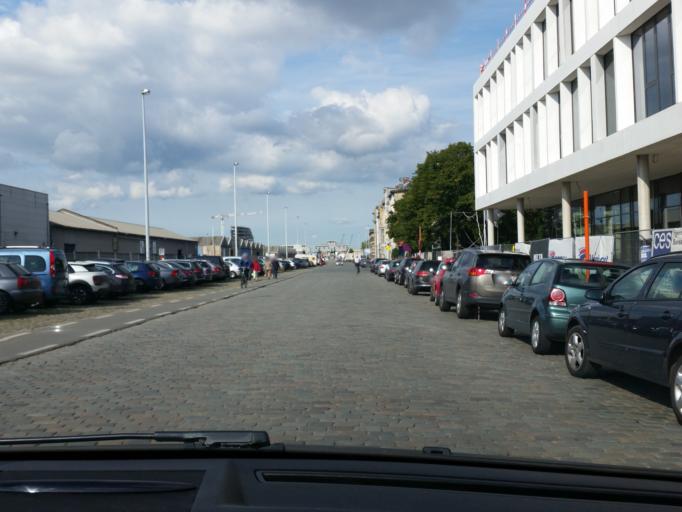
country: BE
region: Flanders
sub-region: Provincie Antwerpen
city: Antwerpen
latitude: 51.2323
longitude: 4.4093
